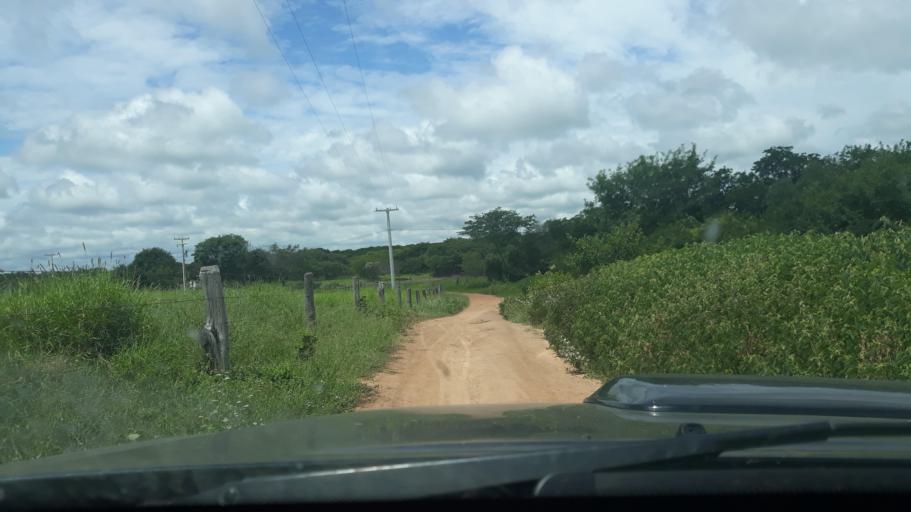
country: BR
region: Bahia
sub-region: Riacho De Santana
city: Riacho de Santana
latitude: -13.8665
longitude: -43.0769
